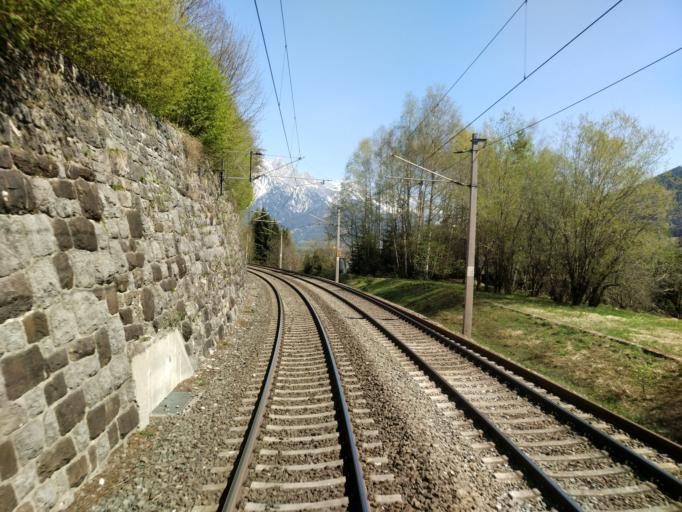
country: AT
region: Salzburg
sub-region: Politischer Bezirk Zell am See
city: Leogang
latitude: 47.4415
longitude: 12.7584
